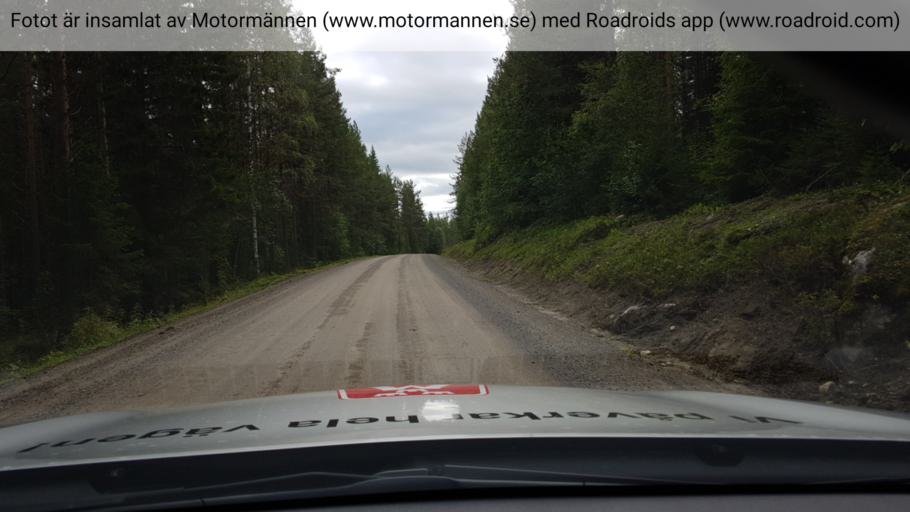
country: SE
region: Jaemtland
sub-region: Ragunda Kommun
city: Hammarstrand
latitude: 62.9475
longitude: 16.1096
